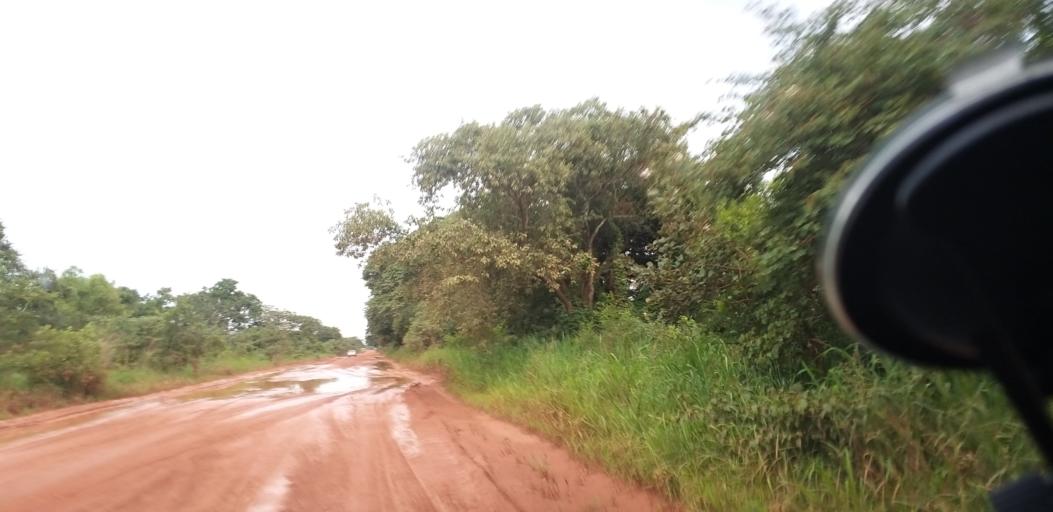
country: ZM
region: Lusaka
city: Lusaka
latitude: -15.2133
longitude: 28.4336
